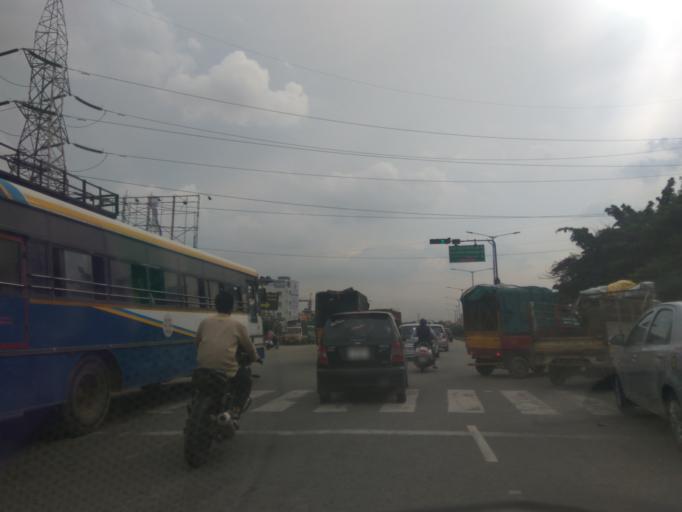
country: IN
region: Karnataka
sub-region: Bangalore Rural
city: Hoskote
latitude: 13.0171
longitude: 77.7047
